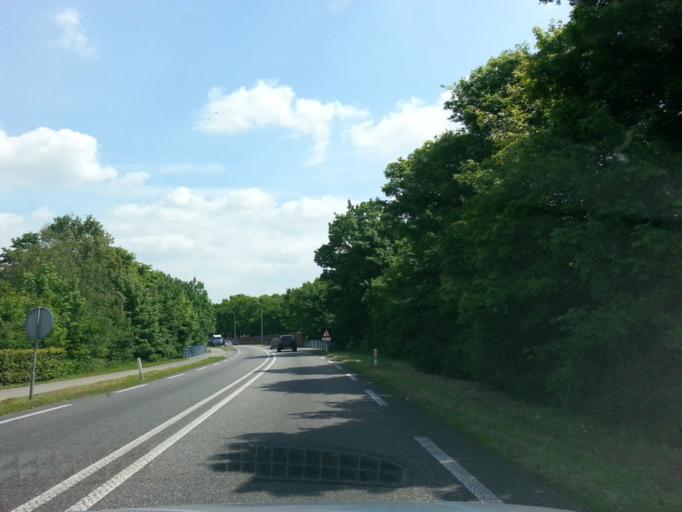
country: NL
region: Gelderland
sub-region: Gemeente Doesburg
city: Doesburg
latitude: 52.0188
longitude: 6.1313
